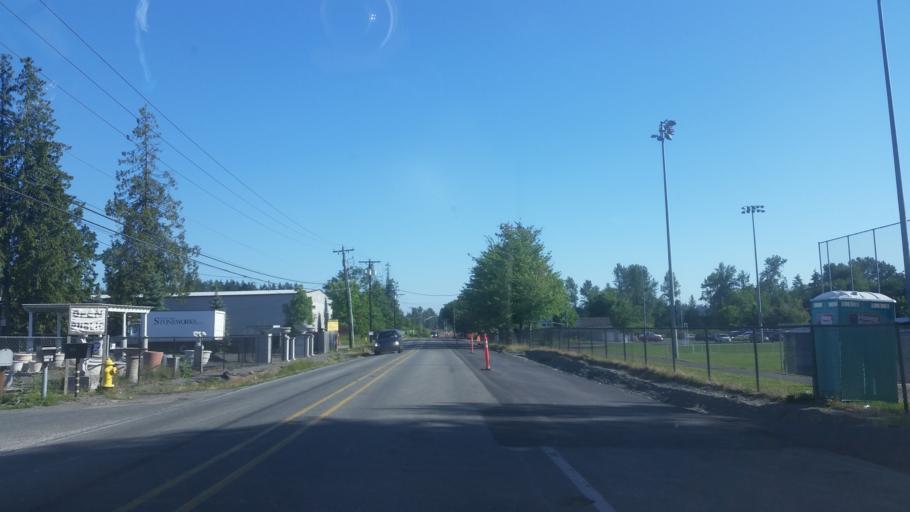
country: US
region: Washington
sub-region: Snohomish County
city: Maltby
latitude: 47.8140
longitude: -122.1100
